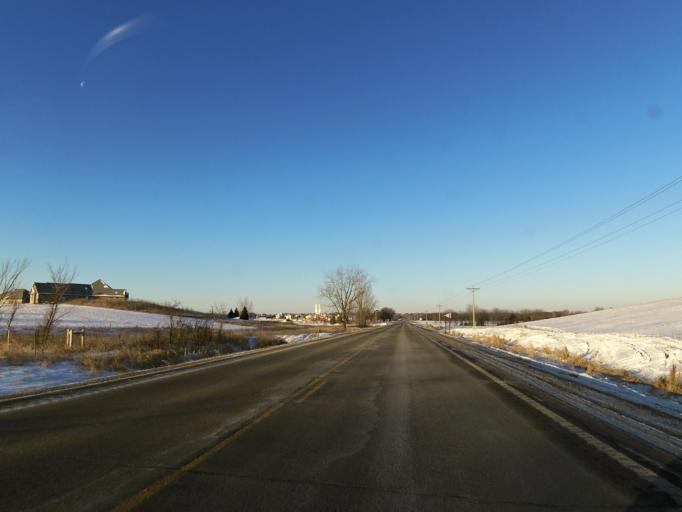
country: US
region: Minnesota
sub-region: Scott County
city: Prior Lake
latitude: 44.6743
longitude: -93.3819
